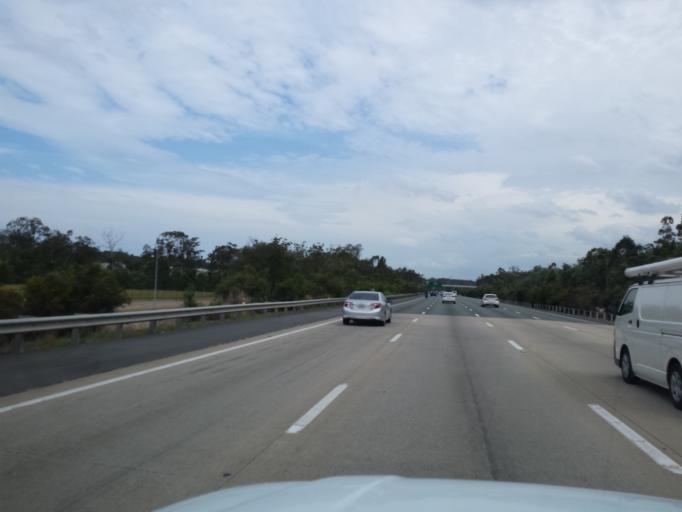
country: AU
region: Queensland
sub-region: Gold Coast
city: Nerang
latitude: -27.9452
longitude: 153.3397
